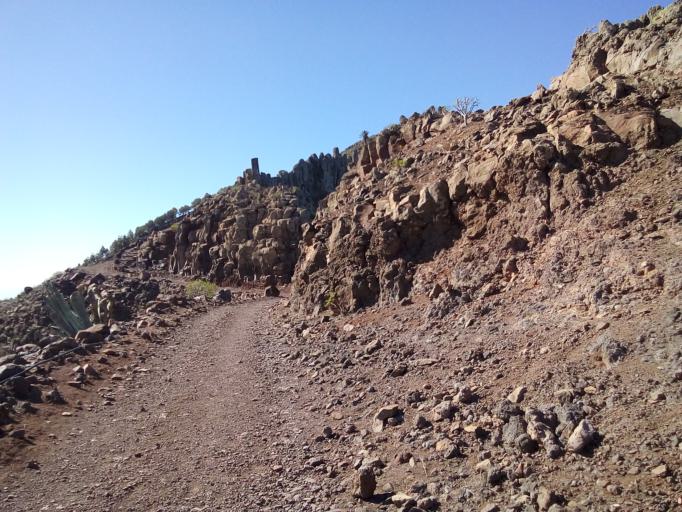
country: ES
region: Canary Islands
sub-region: Provincia de Santa Cruz de Tenerife
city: Vallehermosa
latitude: 28.1220
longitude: -17.3298
